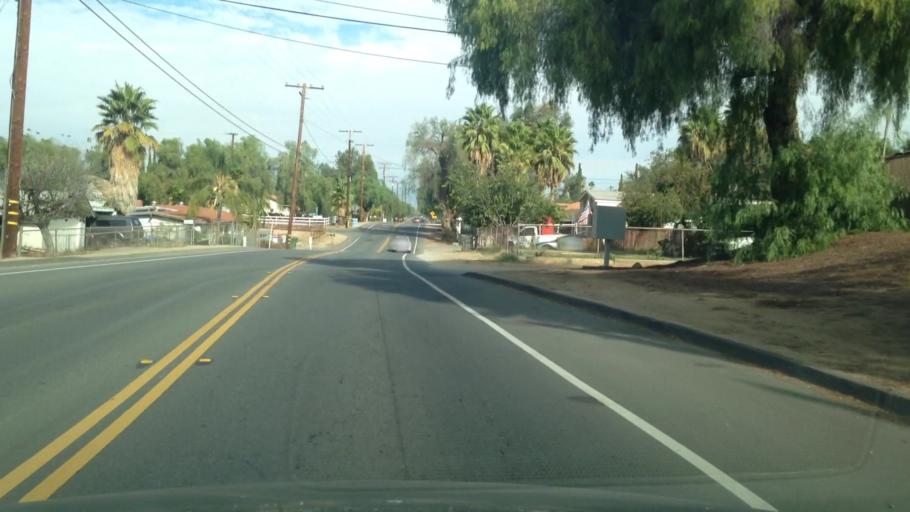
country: US
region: California
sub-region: Riverside County
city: Woodcrest
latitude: 33.8751
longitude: -117.3661
